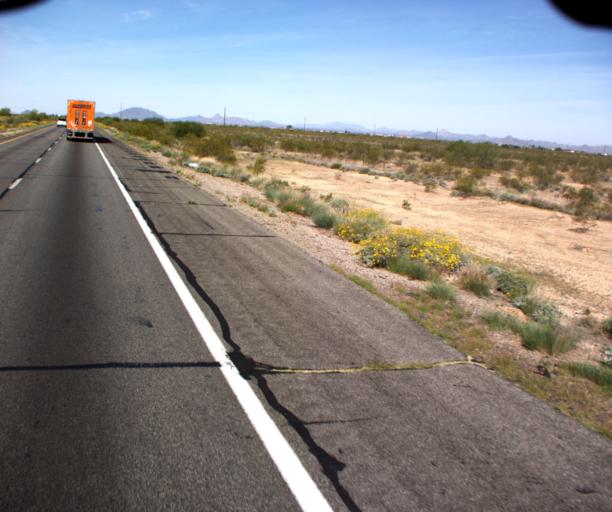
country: US
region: Arizona
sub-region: Maricopa County
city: Buckeye
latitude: 33.4732
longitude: -112.8281
